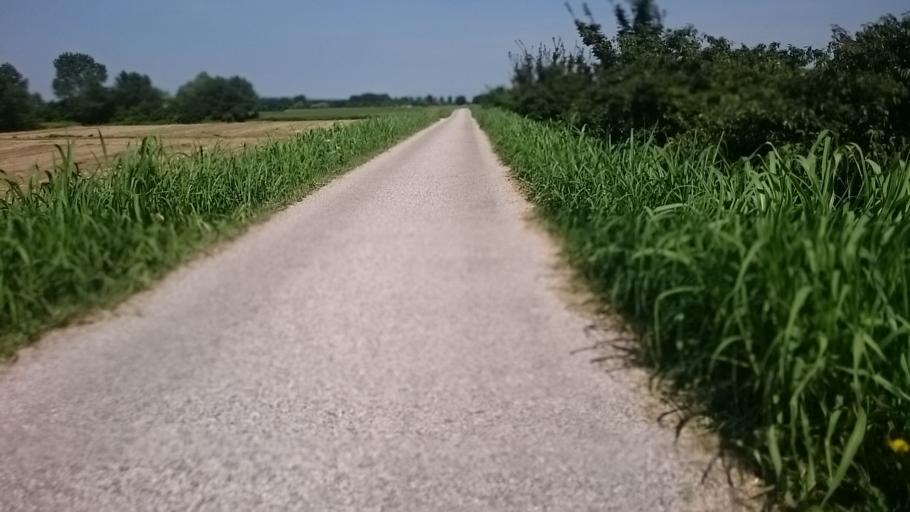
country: IT
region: Veneto
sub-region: Provincia di Padova
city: Saccolongo
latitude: 45.4016
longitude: 11.7665
